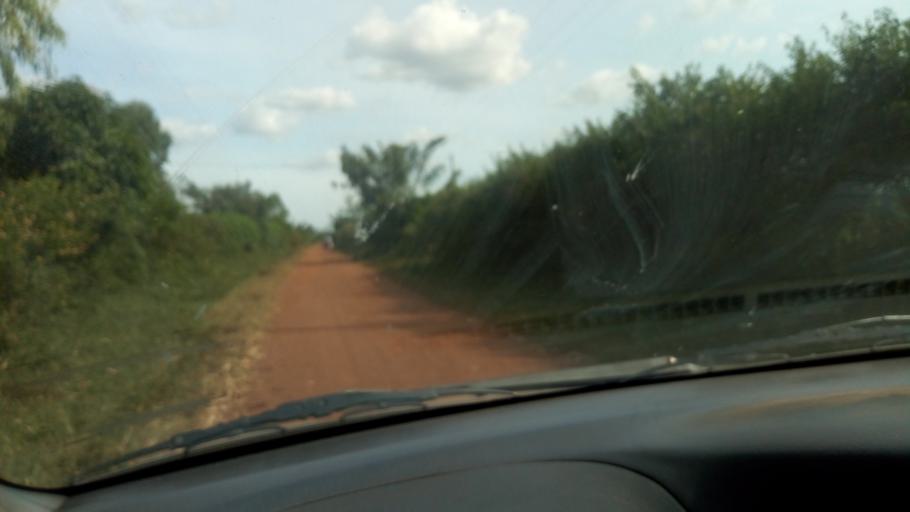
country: UG
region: Western Region
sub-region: Kiryandongo District
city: Kiryandongo
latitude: 1.8150
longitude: 31.9380
